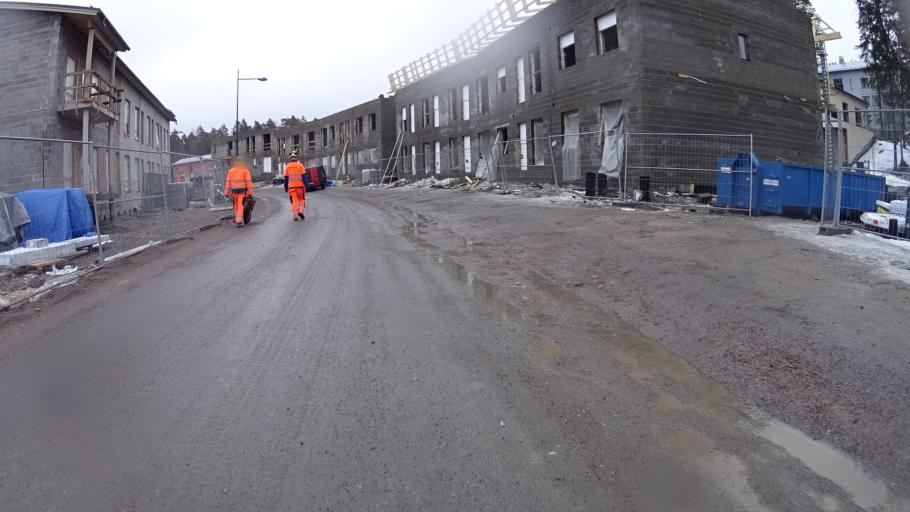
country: FI
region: Uusimaa
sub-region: Helsinki
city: Espoo
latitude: 60.1998
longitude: 24.6068
